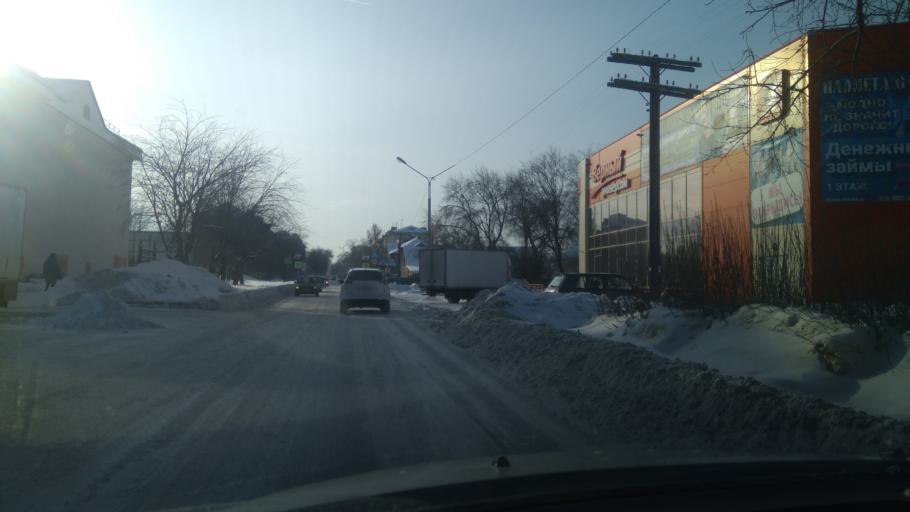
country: RU
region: Sverdlovsk
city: Sukhoy Log
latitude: 56.9057
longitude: 62.0330
